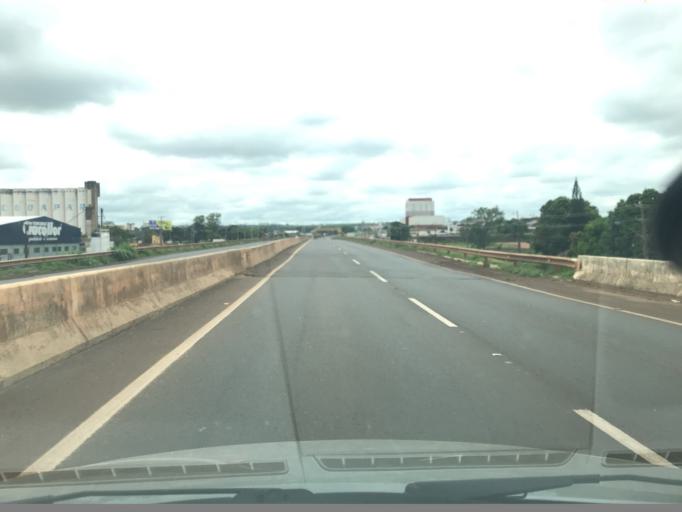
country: BR
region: Parana
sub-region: Paicandu
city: Paicandu
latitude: -23.4505
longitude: -52.0060
